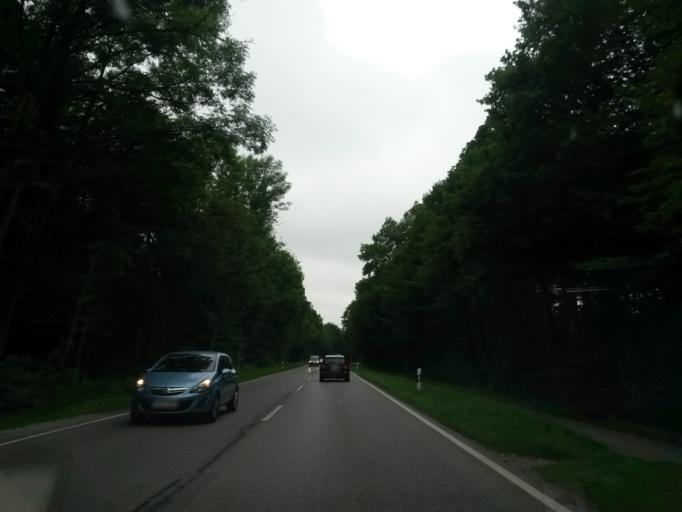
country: DE
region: Bavaria
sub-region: Upper Bavaria
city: Putzbrunn
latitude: 48.0825
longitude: 11.6877
